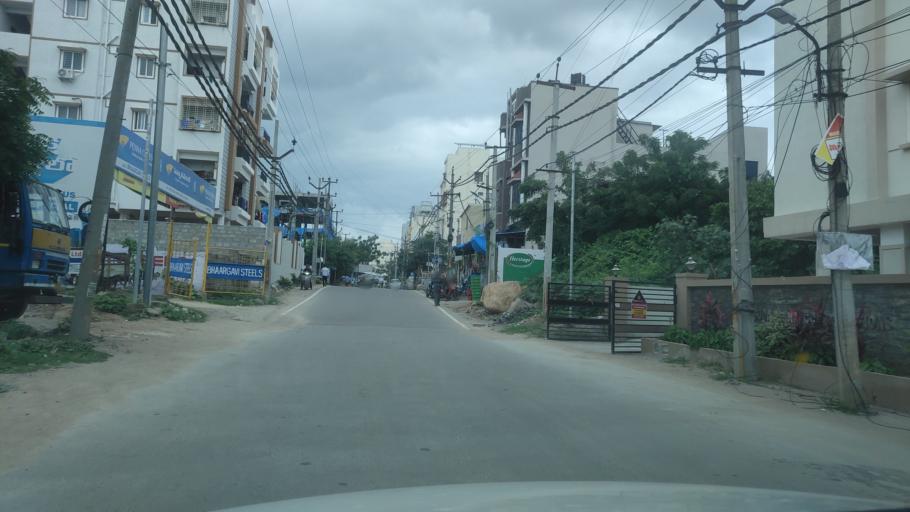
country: IN
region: Telangana
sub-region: Medak
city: Serilingampalle
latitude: 17.4985
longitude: 78.3489
